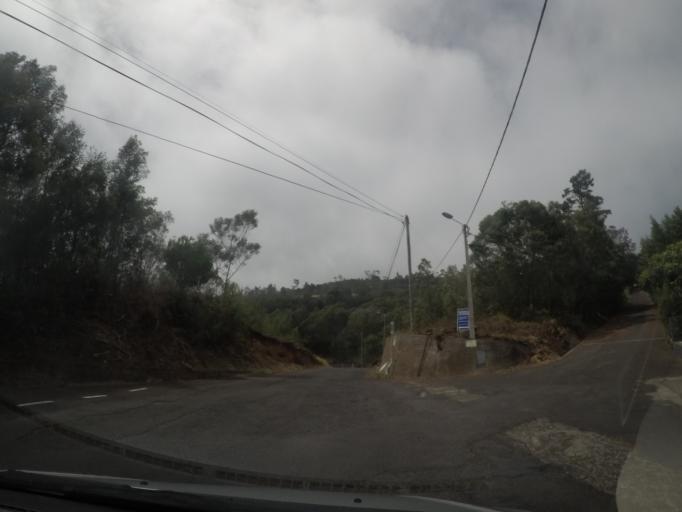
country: PT
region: Madeira
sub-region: Machico
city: Machico
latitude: 32.7022
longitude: -16.7882
